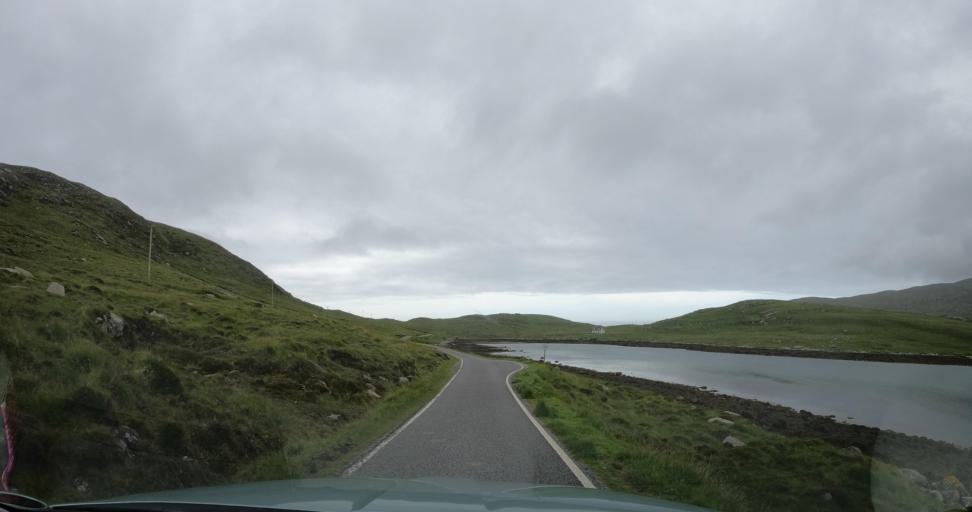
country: GB
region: Scotland
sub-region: Eilean Siar
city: Barra
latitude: 56.9377
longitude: -7.5344
